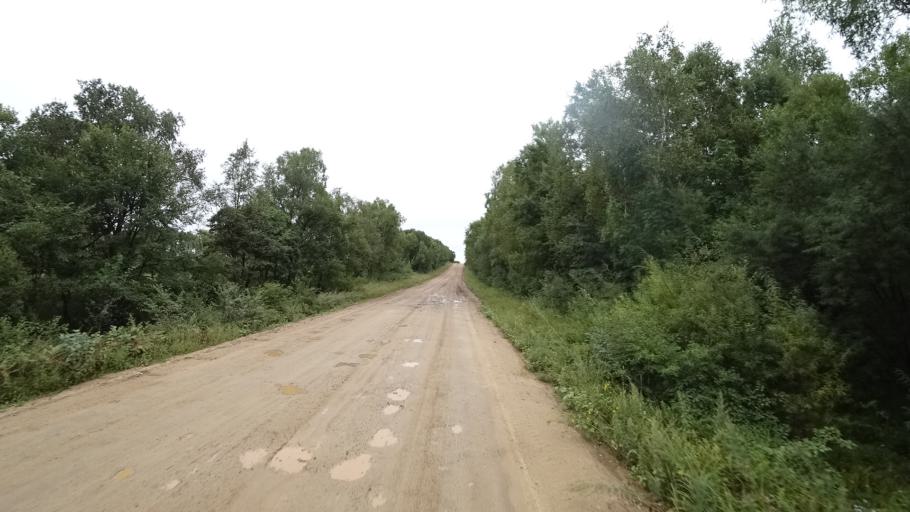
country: RU
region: Primorskiy
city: Ivanovka
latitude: 44.0418
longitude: 132.5404
